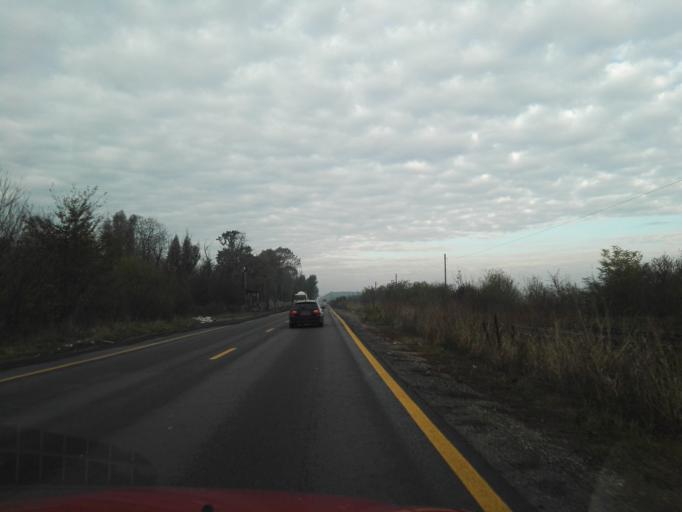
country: RO
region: Ilfov
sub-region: Comuna Jilava
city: Jilava
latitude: 44.3476
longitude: 26.0720
